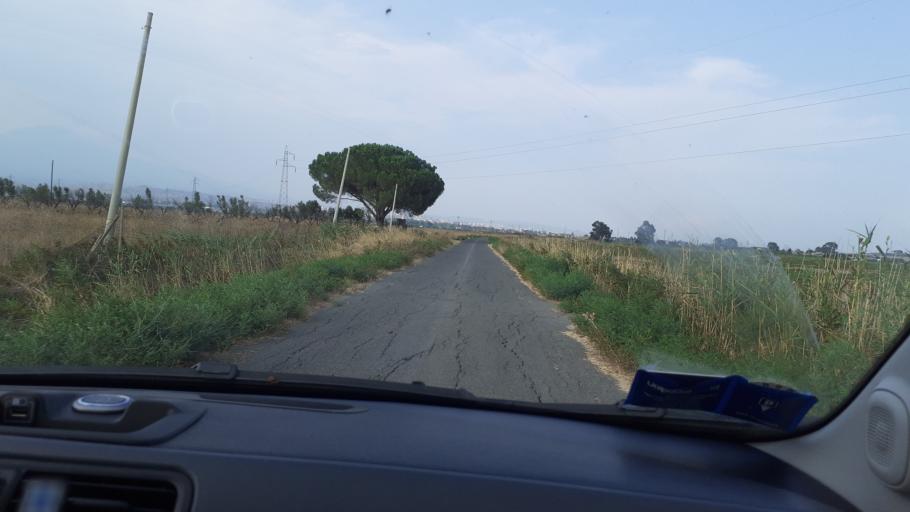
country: IT
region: Sicily
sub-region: Catania
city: Catania
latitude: 37.4283
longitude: 15.0126
